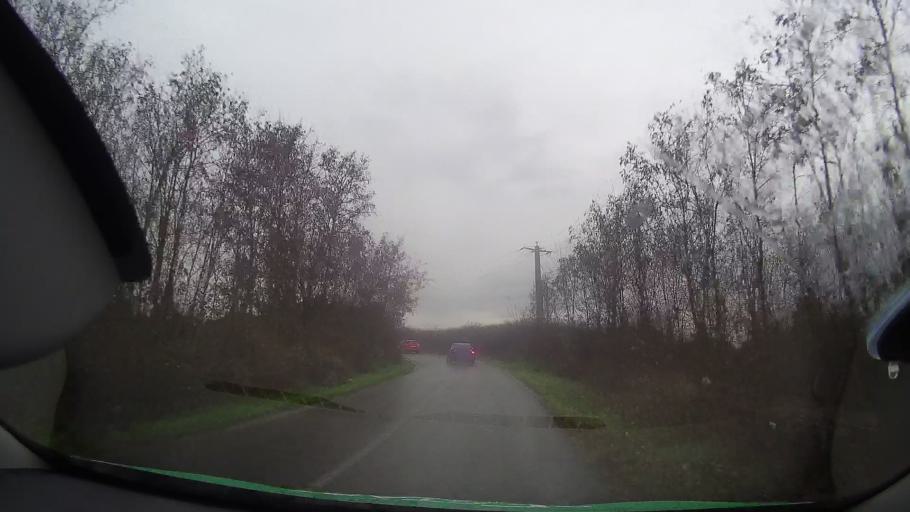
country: RO
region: Bihor
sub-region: Comuna Holod
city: Vintere
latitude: 46.7507
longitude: 22.1448
